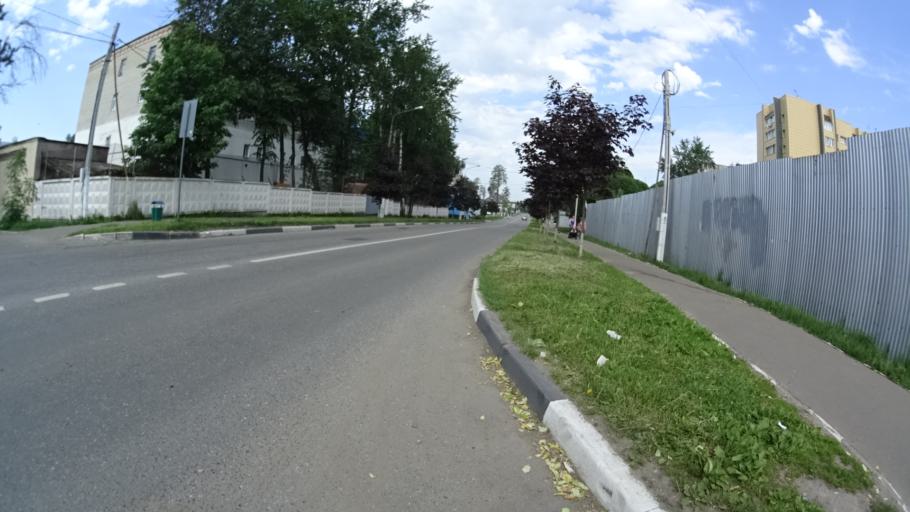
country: RU
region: Moskovskaya
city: Lesnoy
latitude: 56.0813
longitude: 37.9268
